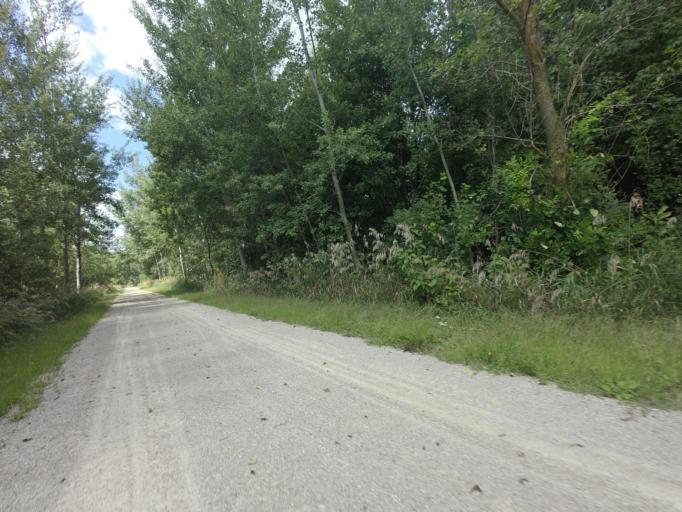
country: CA
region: Ontario
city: North Perth
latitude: 43.6003
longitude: -81.1060
